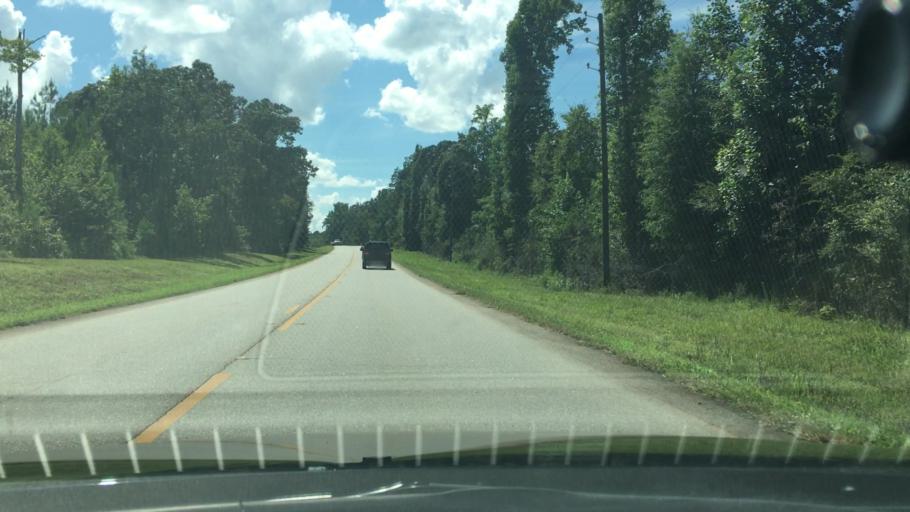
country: US
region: Georgia
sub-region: Jasper County
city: Monticello
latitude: 33.3054
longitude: -83.6061
